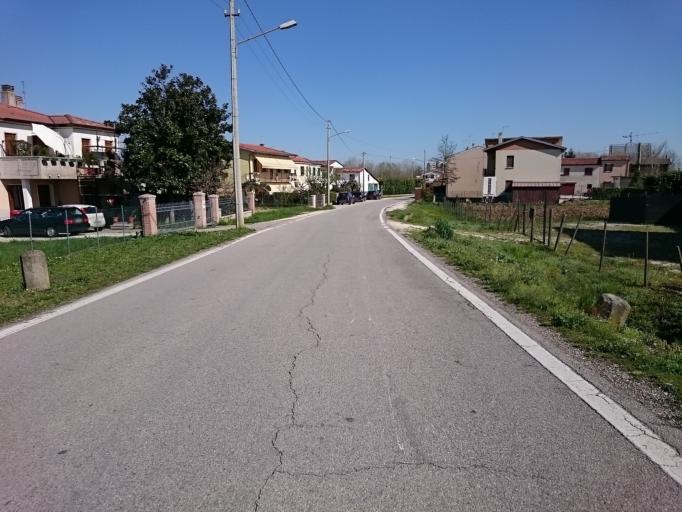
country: IT
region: Veneto
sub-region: Provincia di Padova
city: Ponte San Nicolo
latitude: 45.3944
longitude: 11.9135
